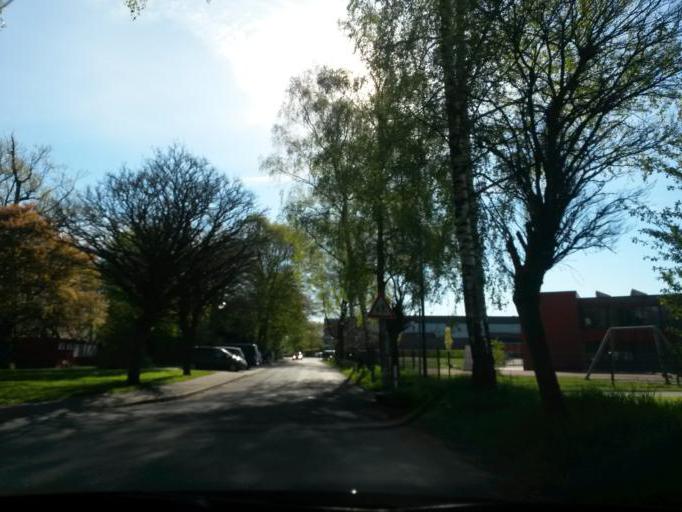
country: DE
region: Schleswig-Holstein
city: Halstenbek
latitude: 53.6331
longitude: 9.8393
